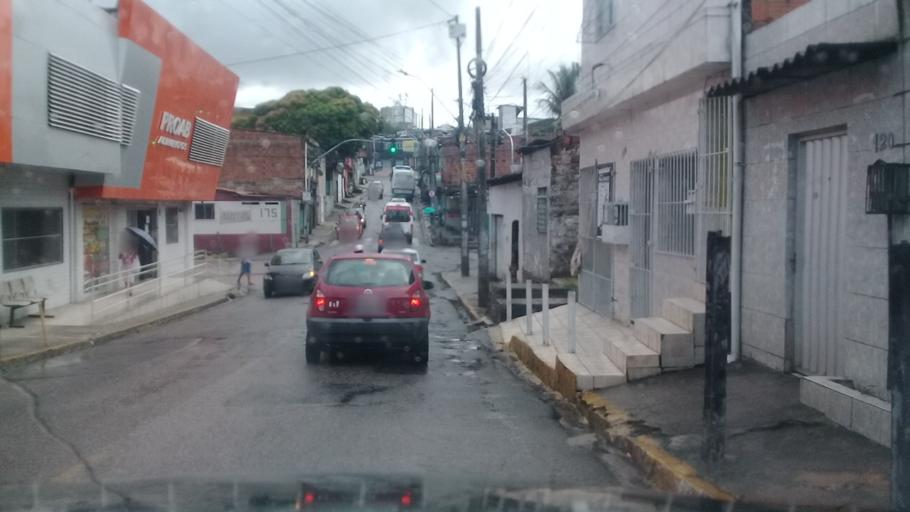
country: BR
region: Pernambuco
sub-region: Jaboatao Dos Guararapes
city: Jaboatao dos Guararapes
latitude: -8.1127
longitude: -34.9526
